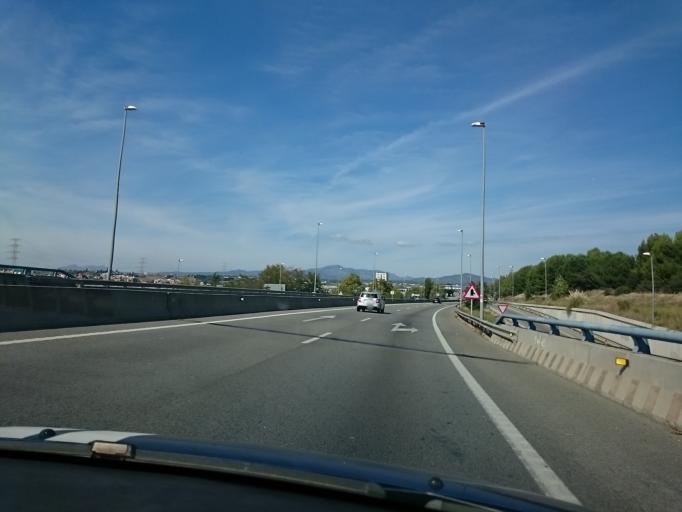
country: ES
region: Catalonia
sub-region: Provincia de Barcelona
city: Santa Perpetua de Mogoda
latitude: 41.5325
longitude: 2.1966
